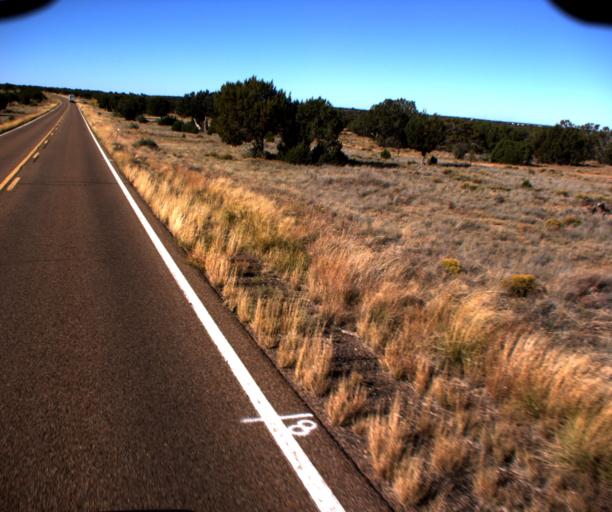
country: US
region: Arizona
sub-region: Navajo County
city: Heber-Overgaard
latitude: 34.5089
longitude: -110.4466
